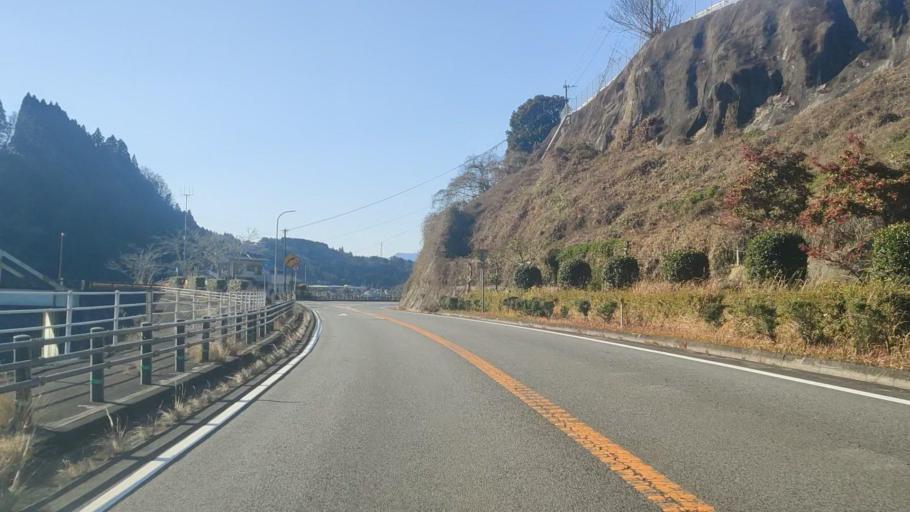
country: JP
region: Oita
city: Usuki
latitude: 33.0698
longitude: 131.6478
